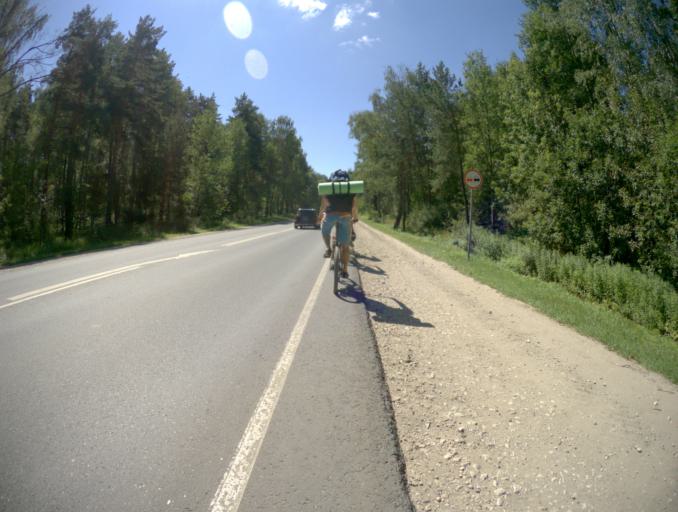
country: RU
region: Nizjnij Novgorod
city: Neklyudovo
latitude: 56.4386
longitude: 43.9989
